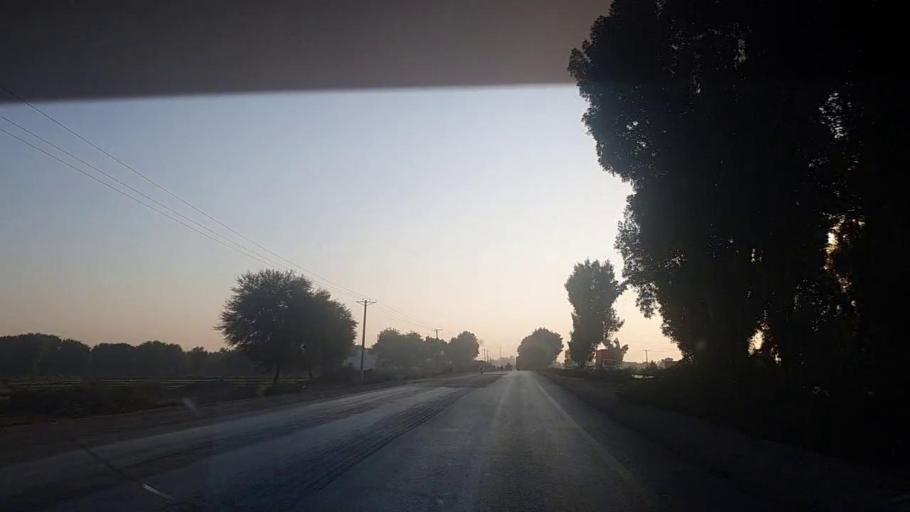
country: PK
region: Sindh
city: Hingorja
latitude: 27.1800
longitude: 68.3992
